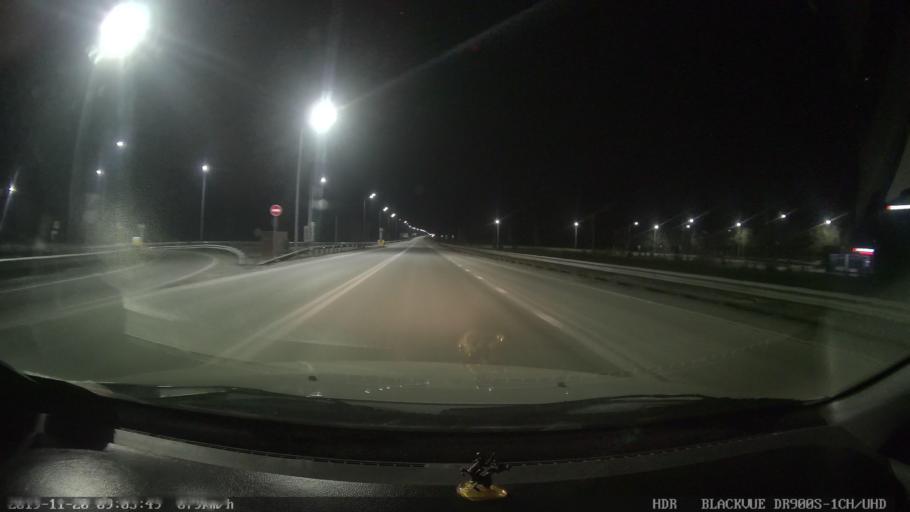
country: RU
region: Tatarstan
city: Stolbishchi
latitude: 55.6795
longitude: 49.1946
